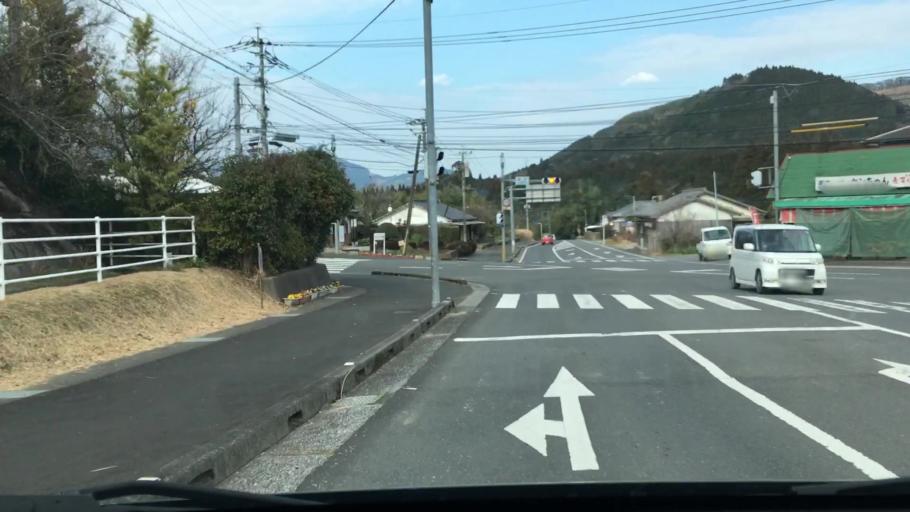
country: JP
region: Miyazaki
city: Kushima
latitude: 31.5261
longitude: 131.2375
